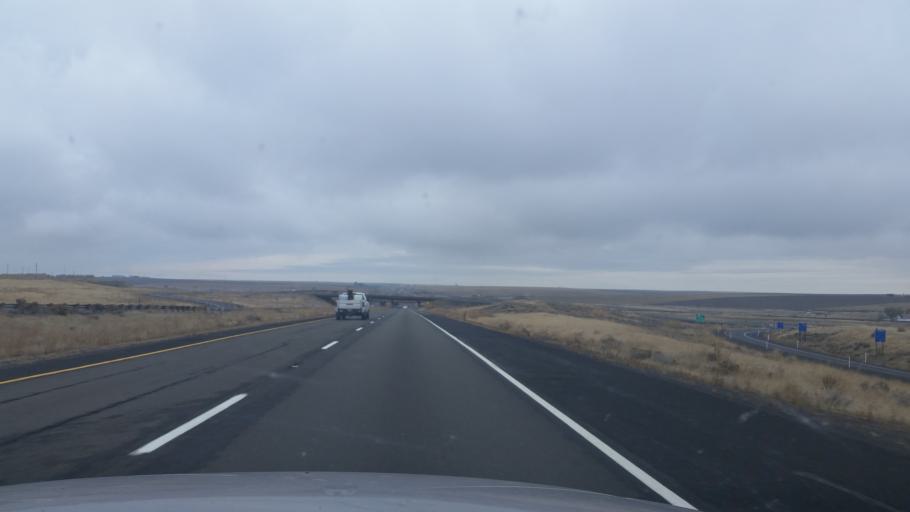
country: US
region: Washington
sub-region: Adams County
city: Ritzville
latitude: 47.1115
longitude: -118.3890
